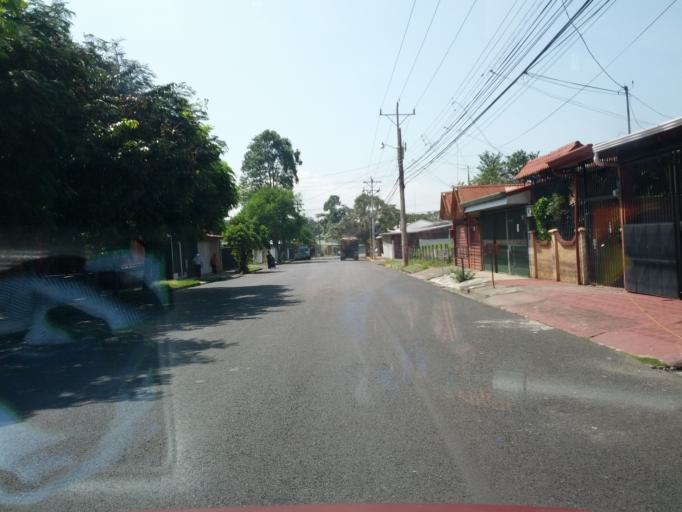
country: CR
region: Alajuela
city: Alajuela
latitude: 10.0134
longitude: -84.2031
